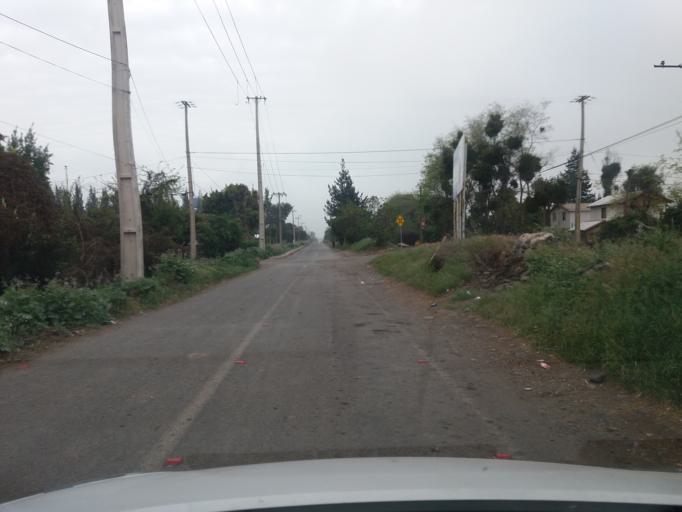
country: CL
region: Valparaiso
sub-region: Provincia de San Felipe
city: Llaillay
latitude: -32.8402
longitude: -71.0632
